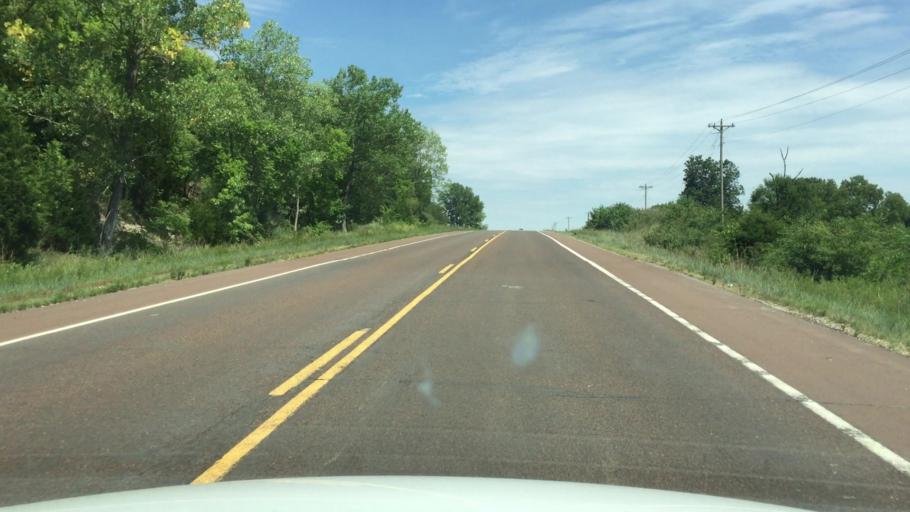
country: US
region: Kansas
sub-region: Douglas County
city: Lawrence
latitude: 38.9713
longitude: -95.3886
